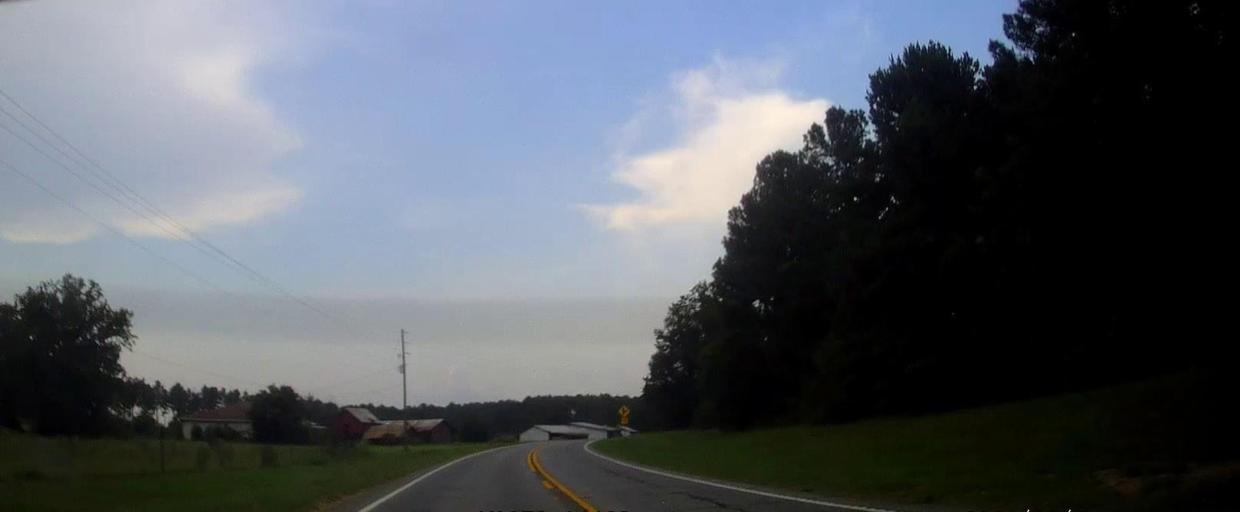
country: US
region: Georgia
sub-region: Laurens County
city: East Dublin
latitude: 32.5781
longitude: -82.8380
